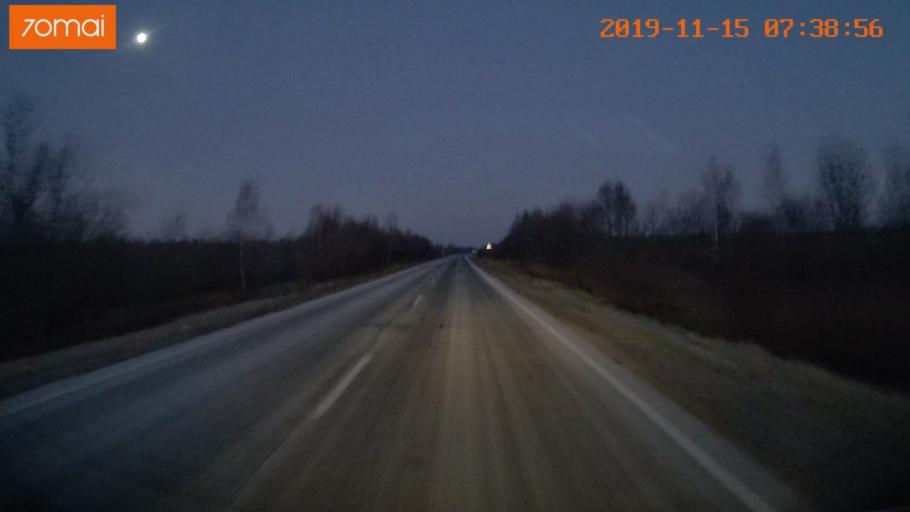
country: RU
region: Vologda
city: Sheksna
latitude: 58.7625
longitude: 38.3903
